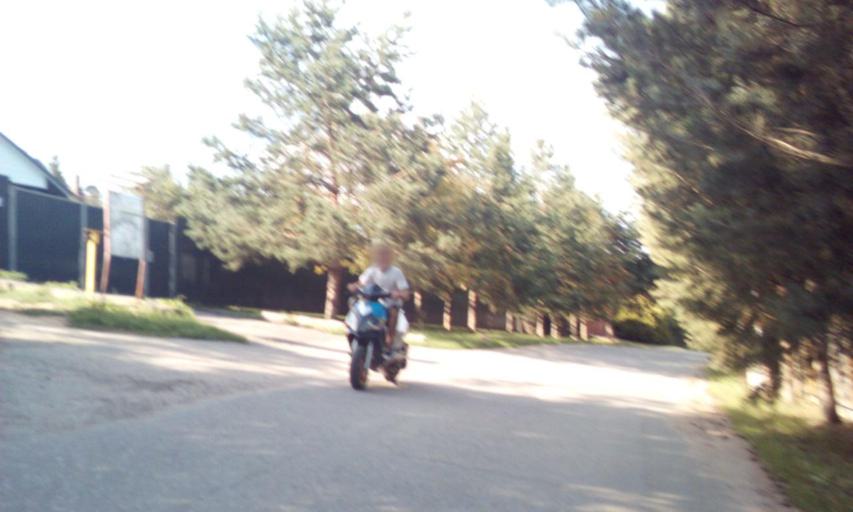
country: RU
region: Moskovskaya
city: Kolyubakino
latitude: 55.6451
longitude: 36.5684
